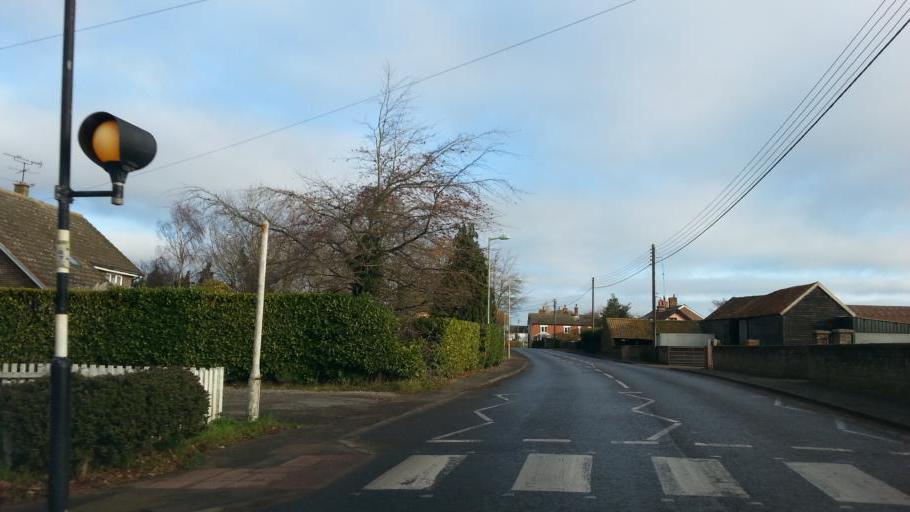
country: GB
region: England
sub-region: Suffolk
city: Wickham Market
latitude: 52.1165
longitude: 1.3836
